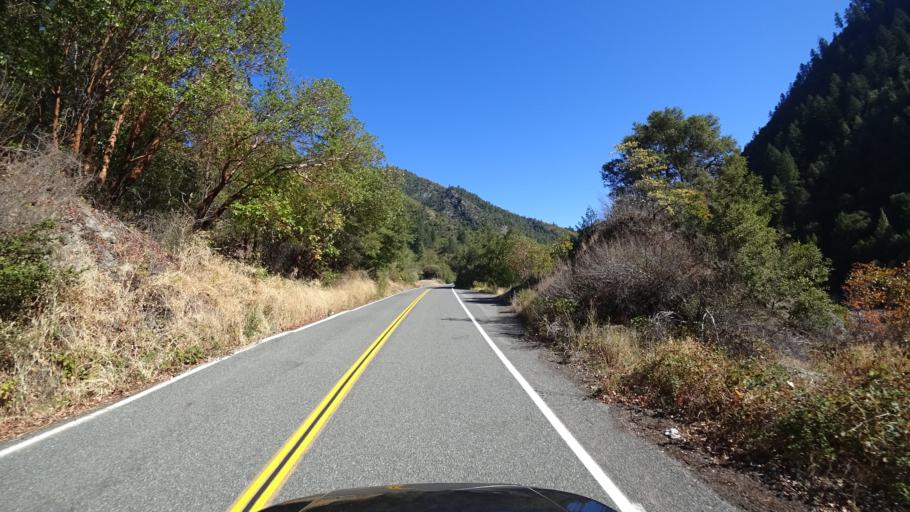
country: US
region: California
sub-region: Siskiyou County
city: Happy Camp
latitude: 41.3790
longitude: -123.4756
